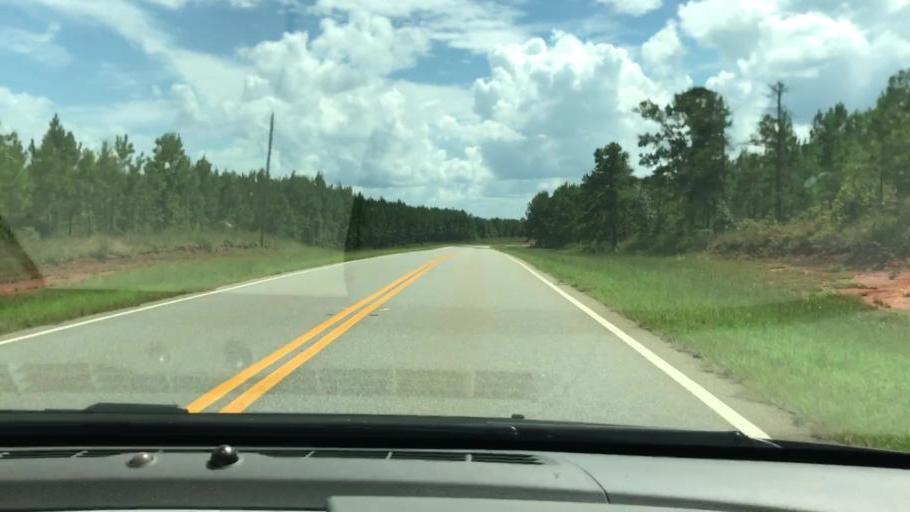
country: US
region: Georgia
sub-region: Quitman County
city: Georgetown
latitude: 31.9175
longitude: -85.0592
